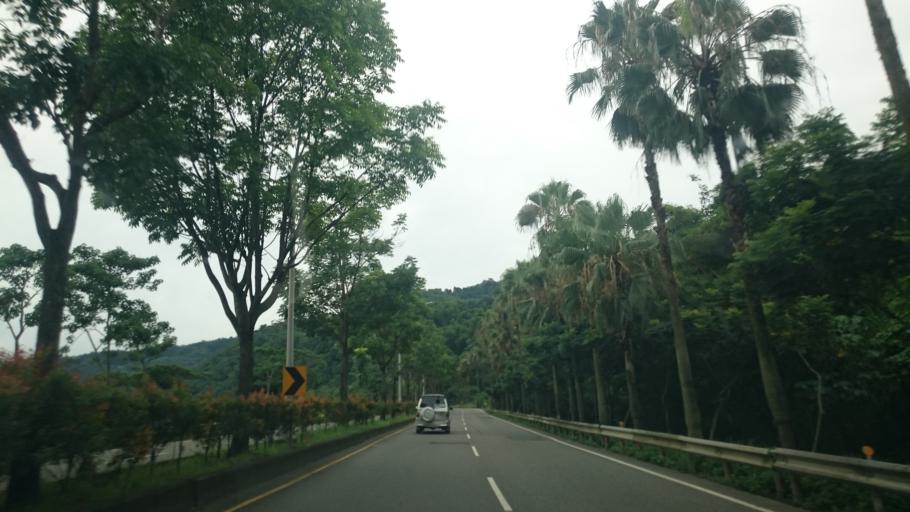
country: TW
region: Taiwan
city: Lugu
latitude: 23.8200
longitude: 120.8413
